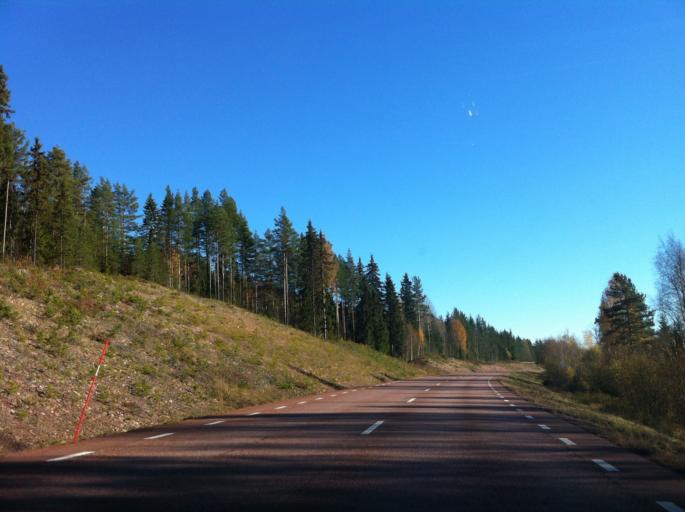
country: SE
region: Dalarna
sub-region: Alvdalens Kommun
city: AElvdalen
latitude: 61.2806
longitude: 13.9478
